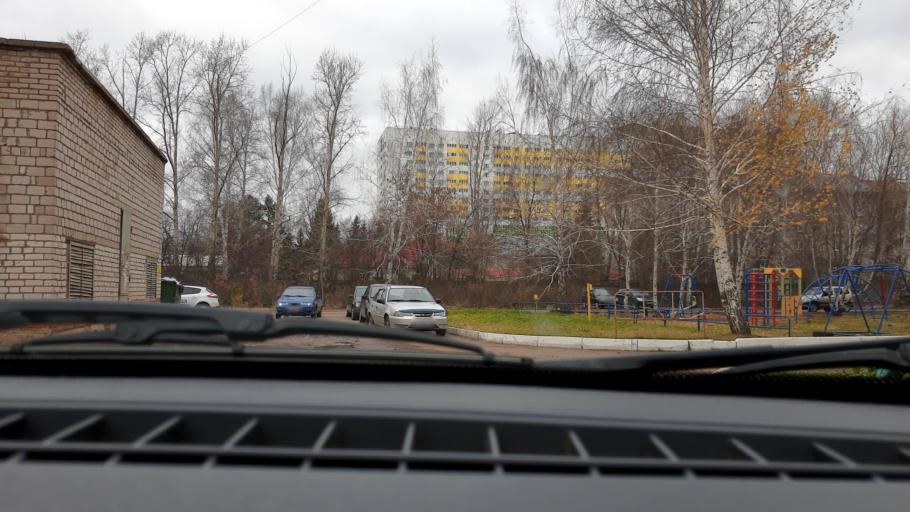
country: RU
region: Bashkortostan
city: Mikhaylovka
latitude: 54.7899
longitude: 55.8674
